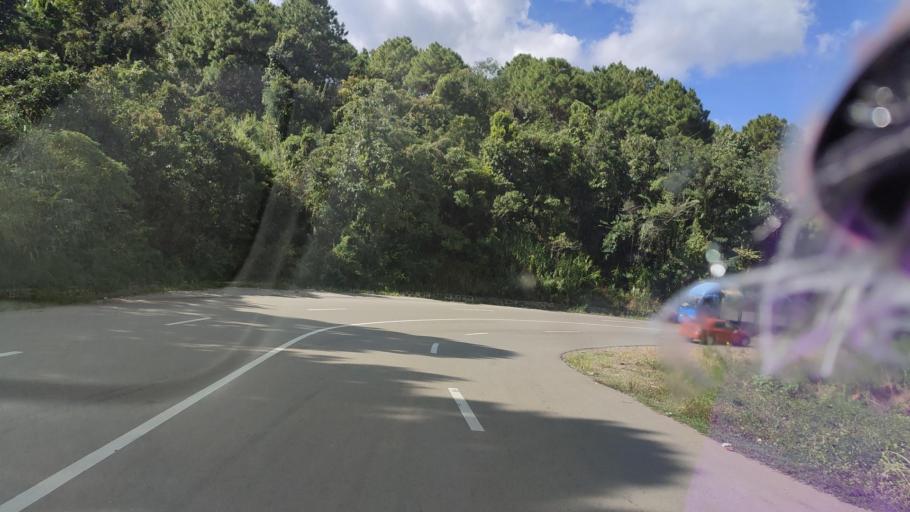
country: MM
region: Mandalay
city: Yamethin
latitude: 20.6499
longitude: 96.5517
